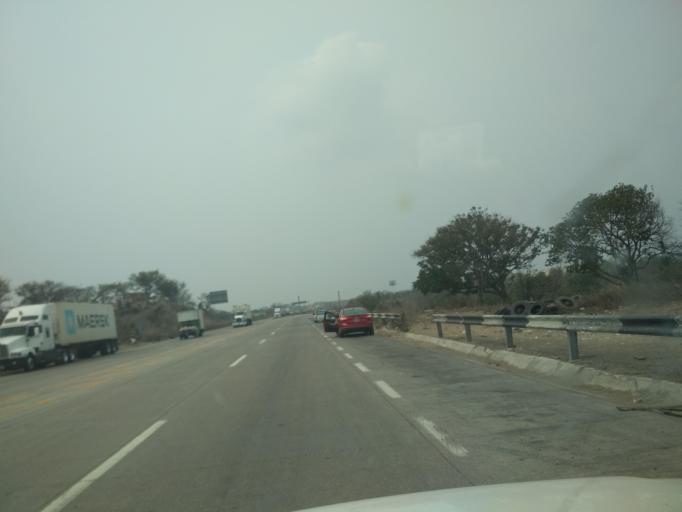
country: MX
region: Veracruz
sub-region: Veracruz
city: Fraccionamiento Geovillas los Pinos
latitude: 19.2149
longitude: -96.2210
